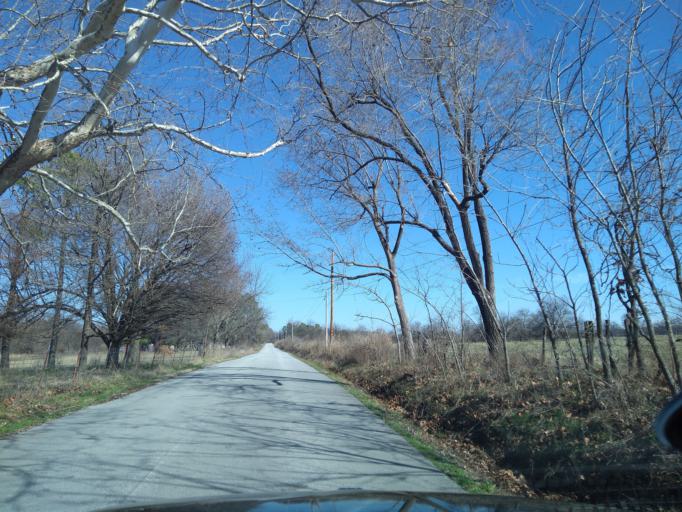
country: US
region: Arkansas
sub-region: Washington County
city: Farmington
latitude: 36.0610
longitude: -94.2486
